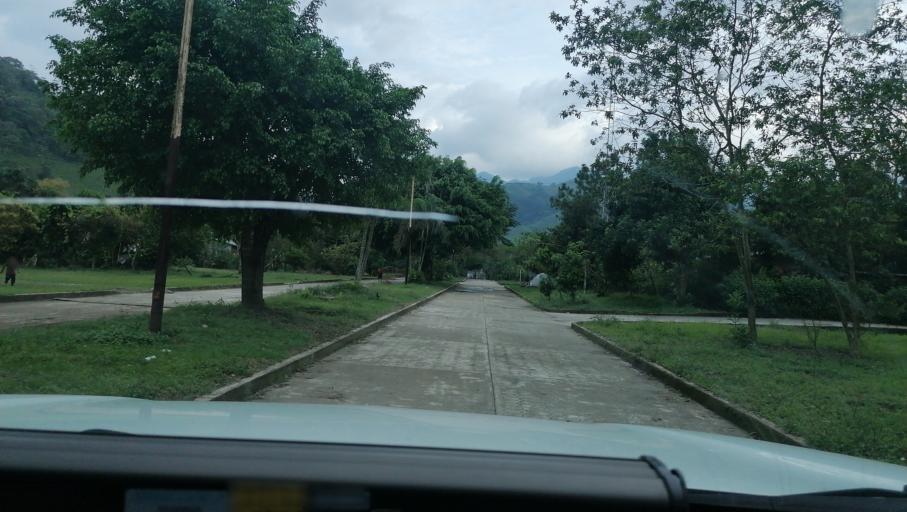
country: MX
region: Chiapas
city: Ixtacomitan
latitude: 17.3406
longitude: -93.1284
